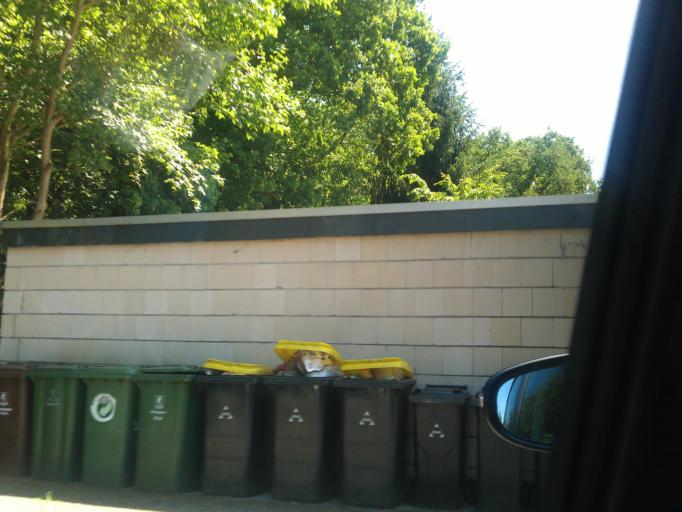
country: DE
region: North Rhine-Westphalia
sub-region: Regierungsbezirk Koln
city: Stossdorf
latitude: 50.8055
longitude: 7.2394
